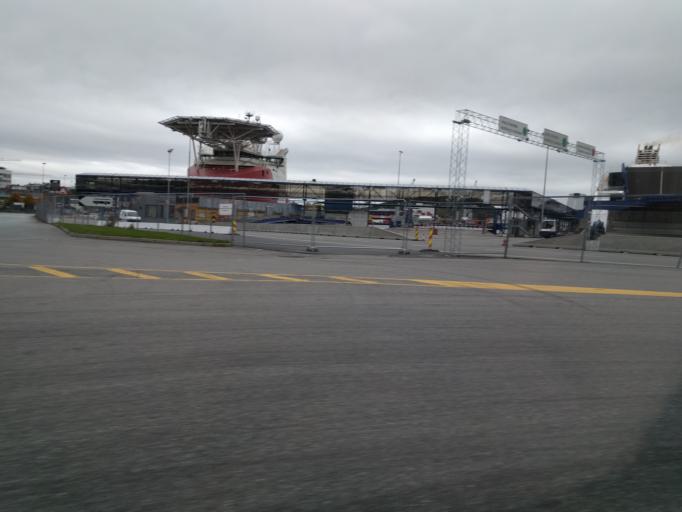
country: NO
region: Vest-Agder
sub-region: Kristiansand
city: Kristiansand
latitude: 58.1452
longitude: 7.9844
